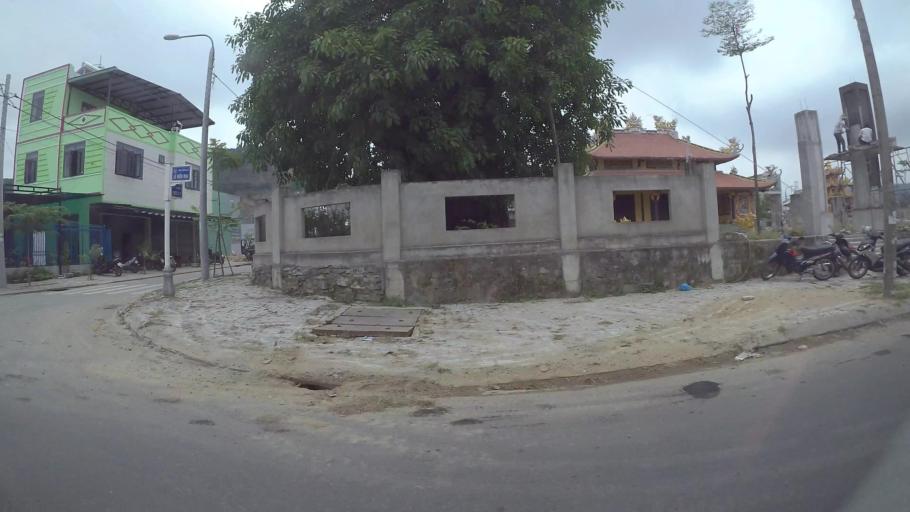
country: VN
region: Da Nang
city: Lien Chieu
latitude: 16.0452
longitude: 108.1658
